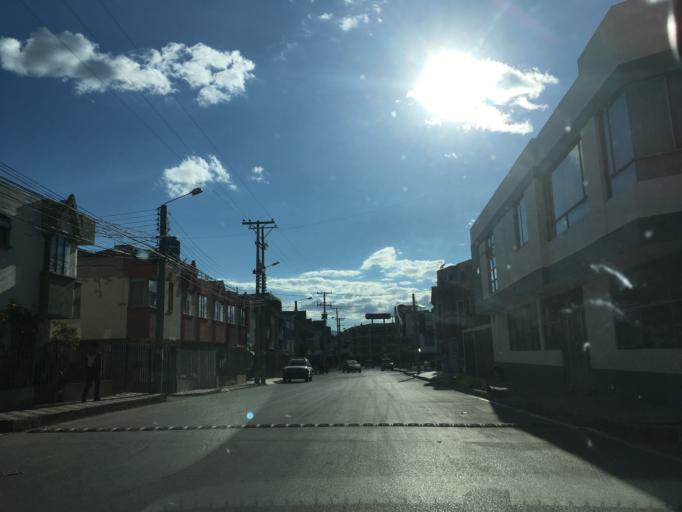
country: CO
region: Boyaca
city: Sogamoso
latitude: 5.7069
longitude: -72.9307
